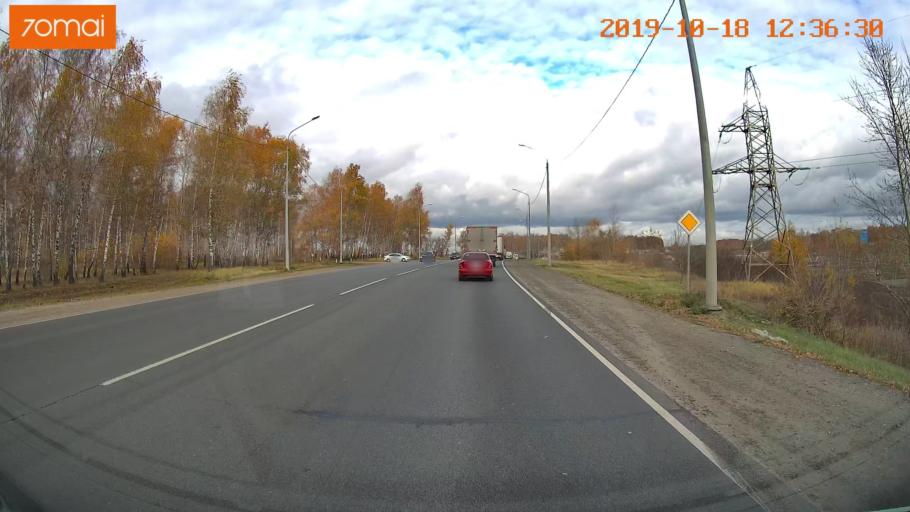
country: RU
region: Rjazan
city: Ryazan'
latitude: 54.6358
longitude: 39.6340
